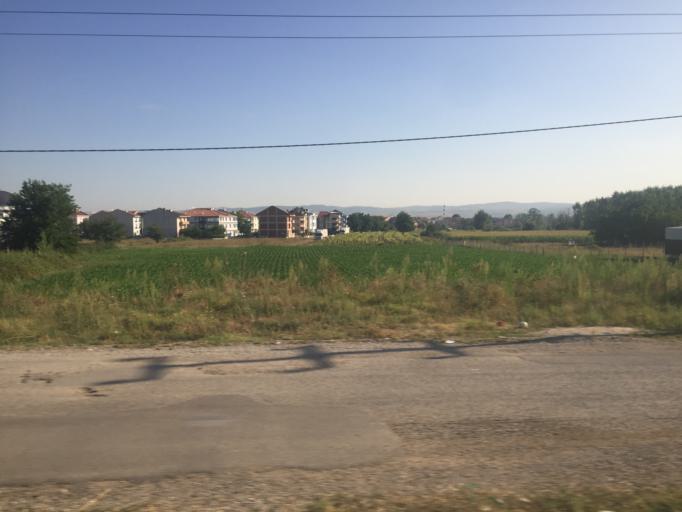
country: TR
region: Bursa
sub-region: Inegoel
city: Inegol
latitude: 40.0756
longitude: 29.5319
